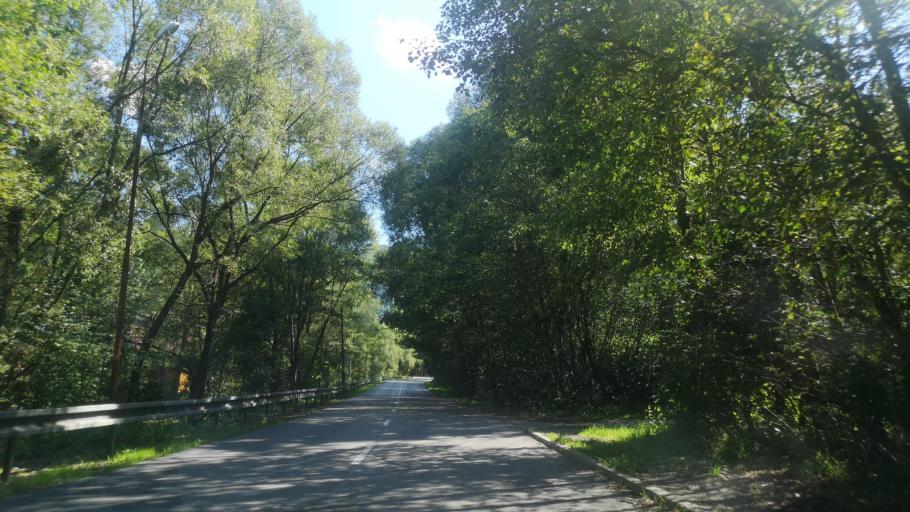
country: SK
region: Zilinsky
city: Oravska Lesna
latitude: 49.2695
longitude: 19.1498
